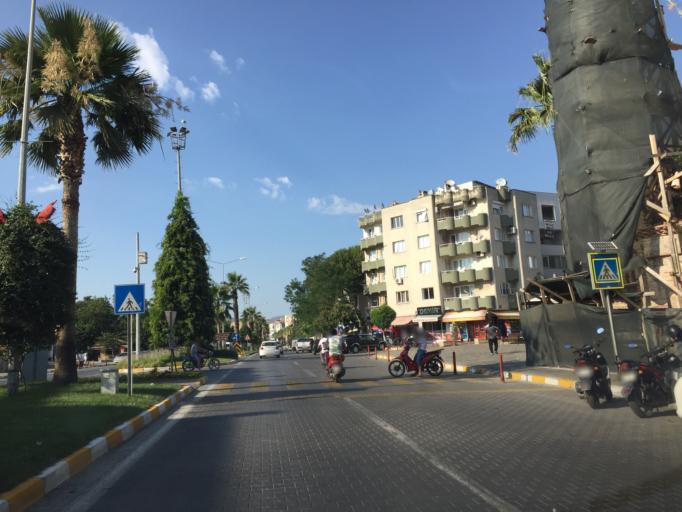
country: TR
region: Izmir
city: Selcuk
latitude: 37.9505
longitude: 27.3698
